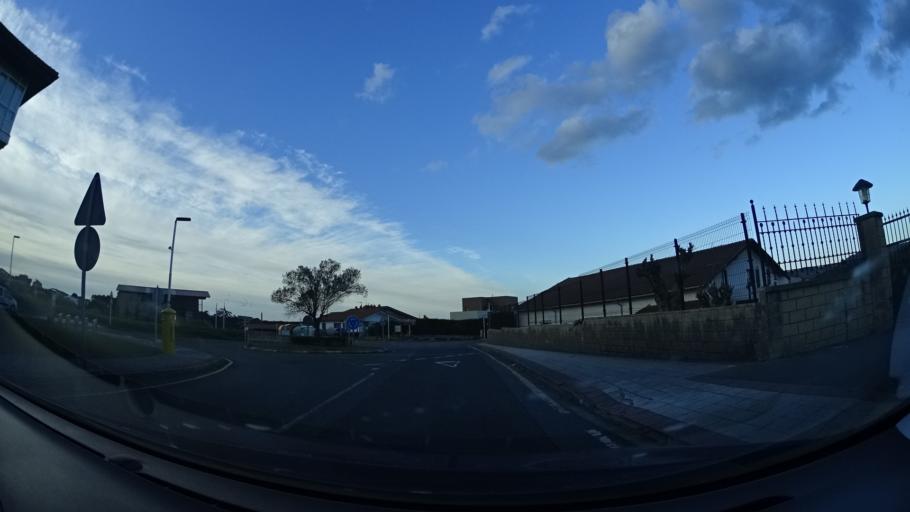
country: ES
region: Basque Country
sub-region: Bizkaia
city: Plentzia
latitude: 43.4062
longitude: -2.9619
